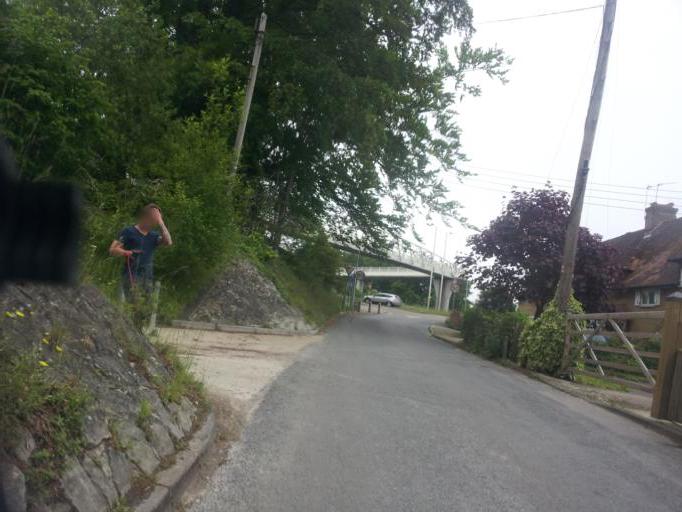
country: GB
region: England
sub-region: Kent
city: Boxley
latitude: 51.2970
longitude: 0.5672
